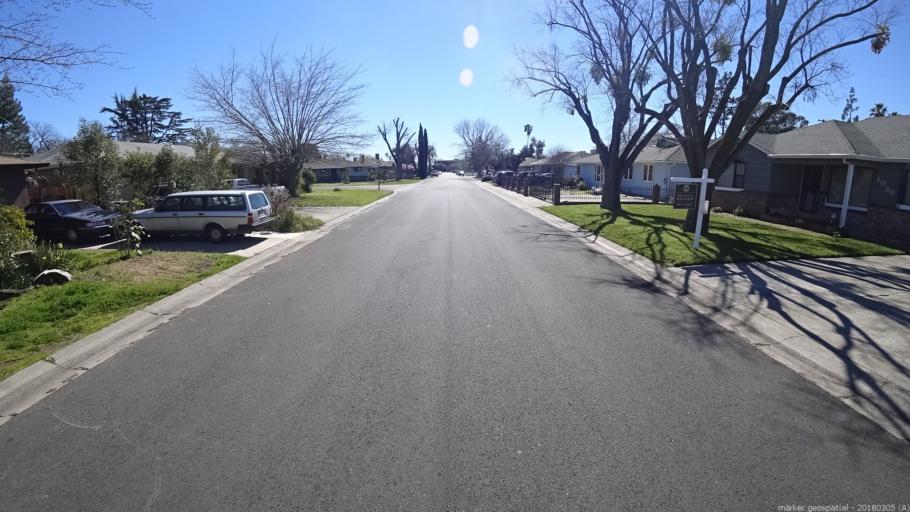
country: US
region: California
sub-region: Sacramento County
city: Florin
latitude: 38.4985
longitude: -121.4154
